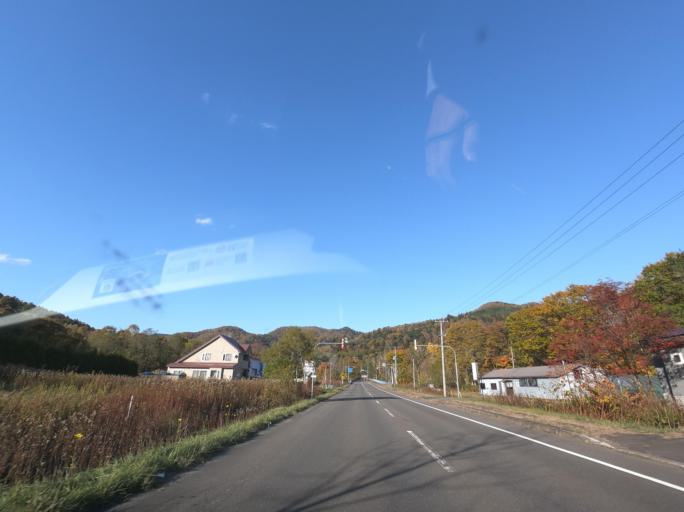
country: JP
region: Hokkaido
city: Iwamizawa
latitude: 43.0037
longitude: 142.0055
